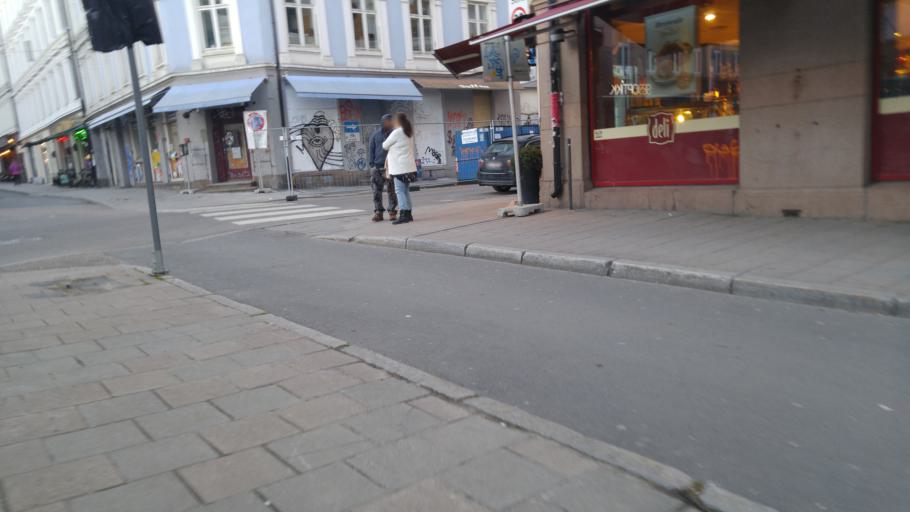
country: NO
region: Oslo
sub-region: Oslo
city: Oslo
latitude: 59.9244
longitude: 10.7592
